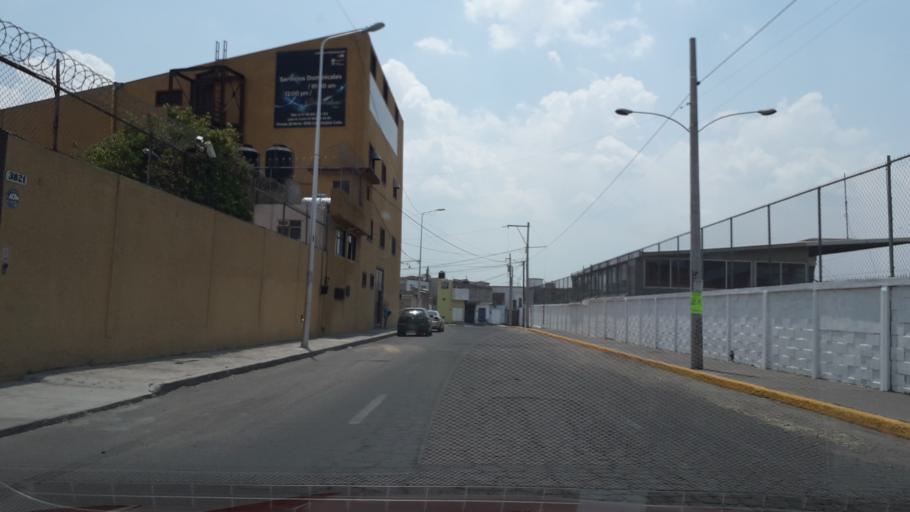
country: MX
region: Puebla
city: Puebla
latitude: 19.0475
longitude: -98.1676
